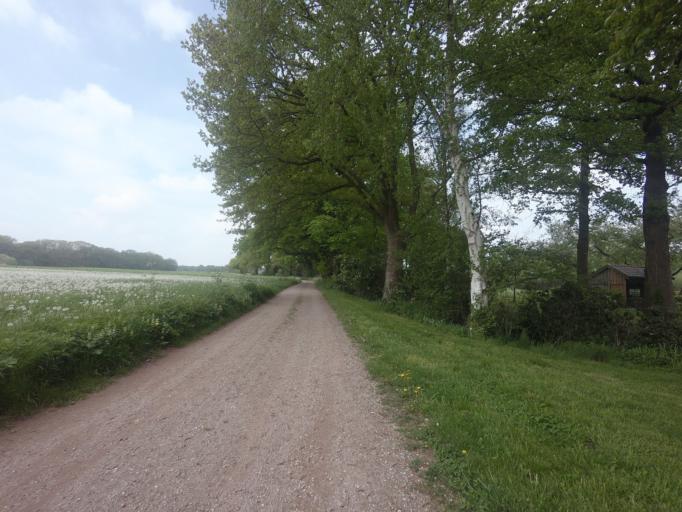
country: NL
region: Overijssel
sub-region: Gemeente Hof van Twente
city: Delden
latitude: 52.2126
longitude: 6.7311
